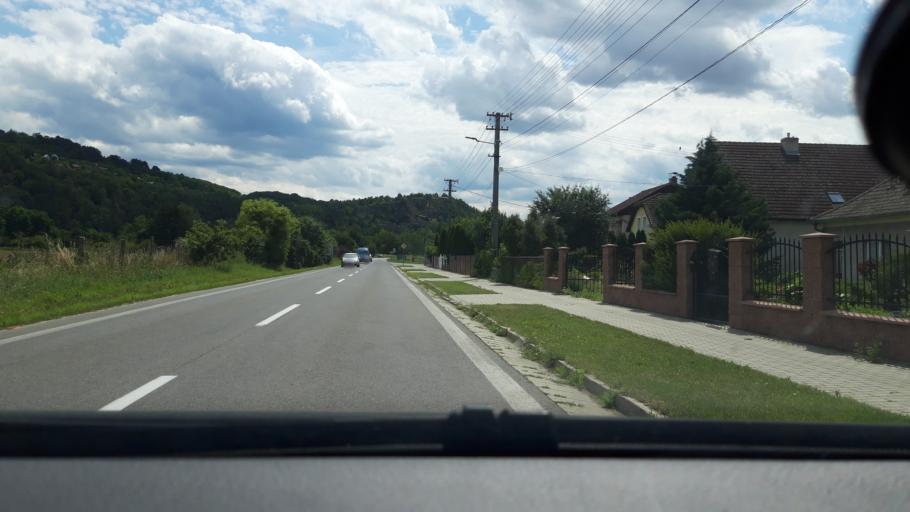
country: SK
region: Trenciansky
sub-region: Okres Nove Mesto nad Vahom
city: Nove Mesto nad Vahom
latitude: 48.7847
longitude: 17.8940
